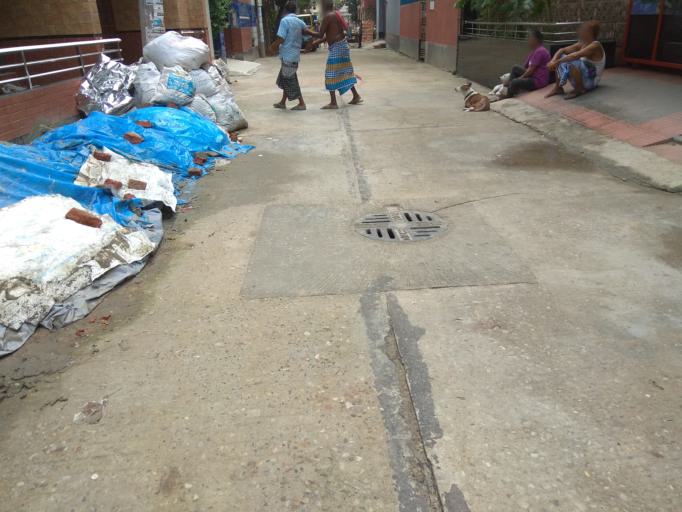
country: BD
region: Dhaka
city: Azimpur
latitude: 23.8043
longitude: 90.3542
